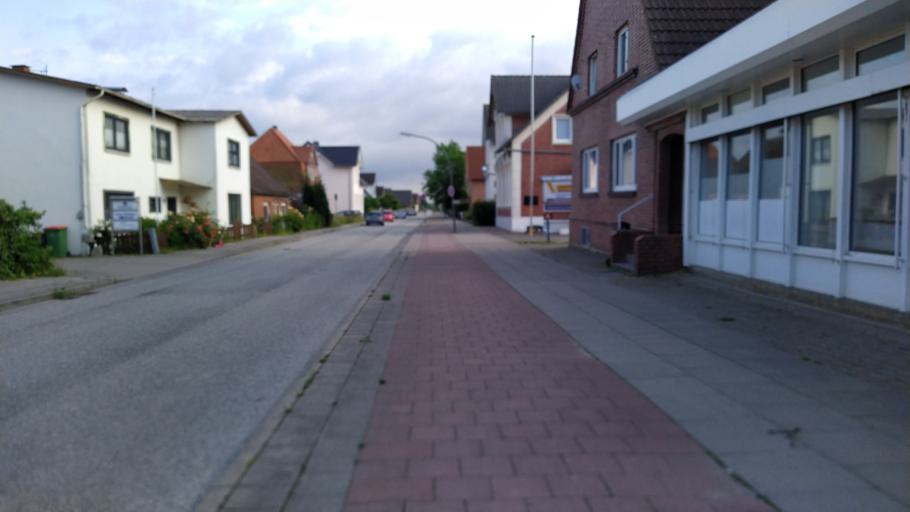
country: DE
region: Lower Saxony
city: Neu Wulmstorf
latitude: 53.5203
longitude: 9.8118
